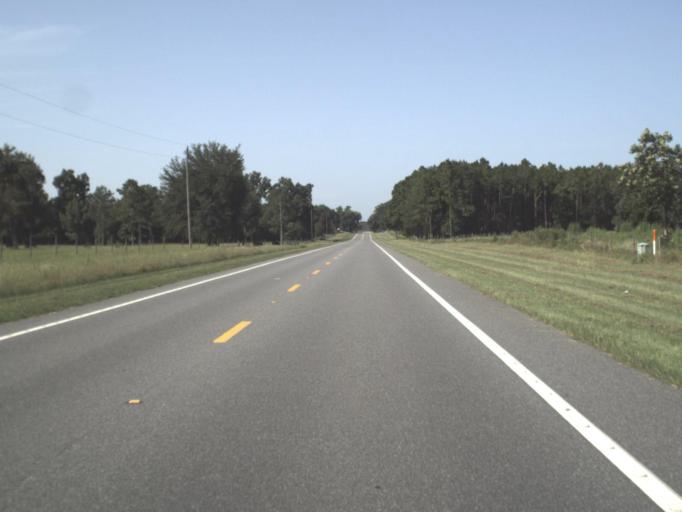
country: US
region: Florida
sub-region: Alachua County
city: High Springs
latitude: 29.9024
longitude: -82.7234
